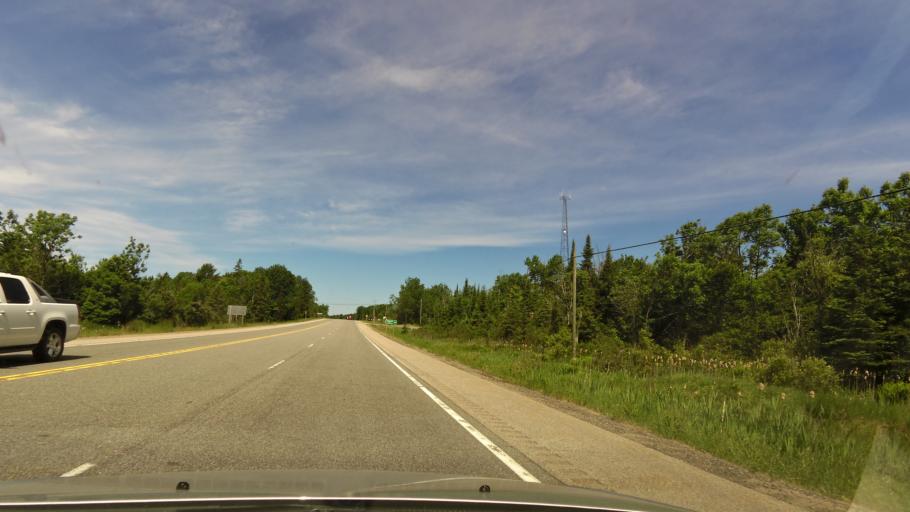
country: CA
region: Ontario
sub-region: Parry Sound District
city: Parry Sound
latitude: 45.5543
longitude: -80.2940
